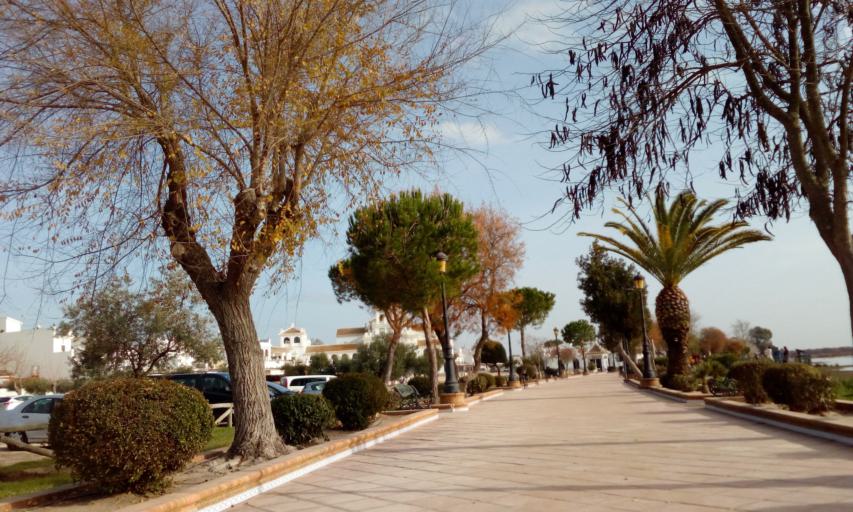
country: ES
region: Andalusia
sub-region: Provincia de Huelva
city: Almonte
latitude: 37.1312
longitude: -6.4871
